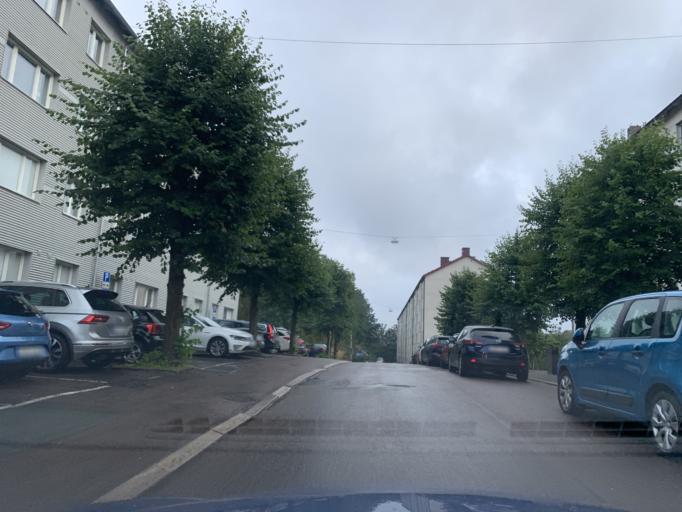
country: SE
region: Vaestra Goetaland
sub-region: Goteborg
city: Goeteborg
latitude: 57.7123
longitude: 12.0124
